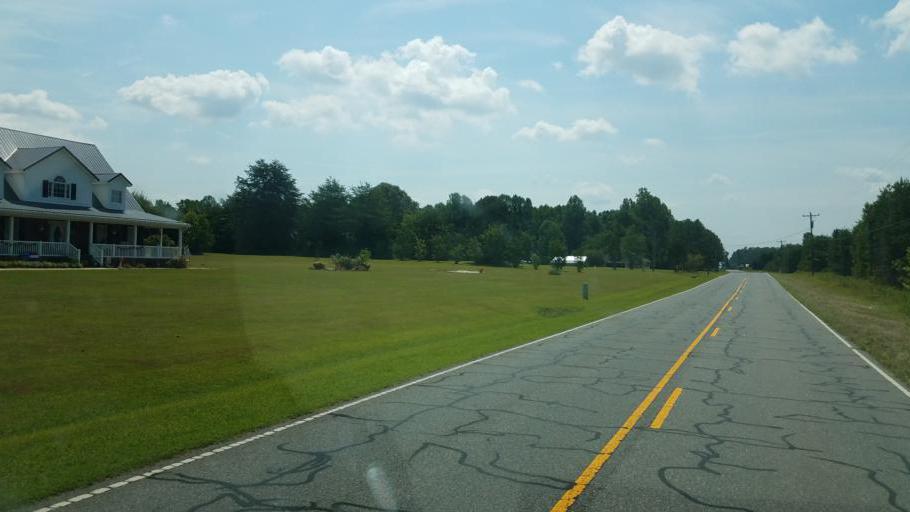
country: US
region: North Carolina
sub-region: Gaston County
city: Cherryville
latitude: 35.4462
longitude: -81.4280
